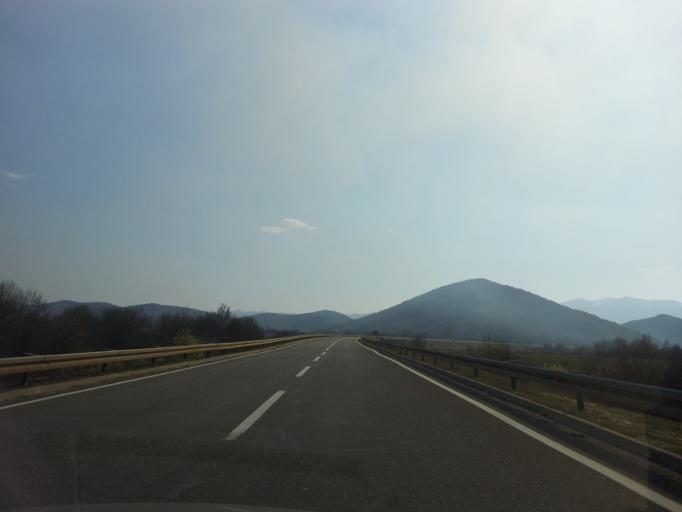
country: HR
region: Zadarska
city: Gracac
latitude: 44.4548
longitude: 15.6695
